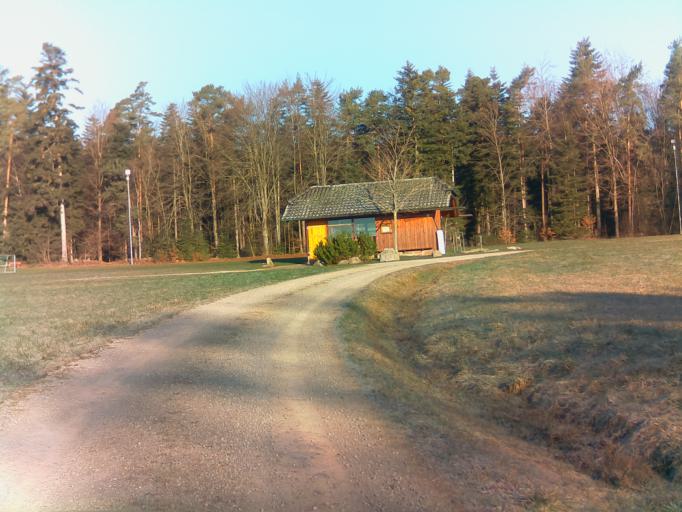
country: DE
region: Baden-Wuerttemberg
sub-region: Karlsruhe Region
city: Oberreichenbach
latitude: 48.7387
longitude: 8.6564
